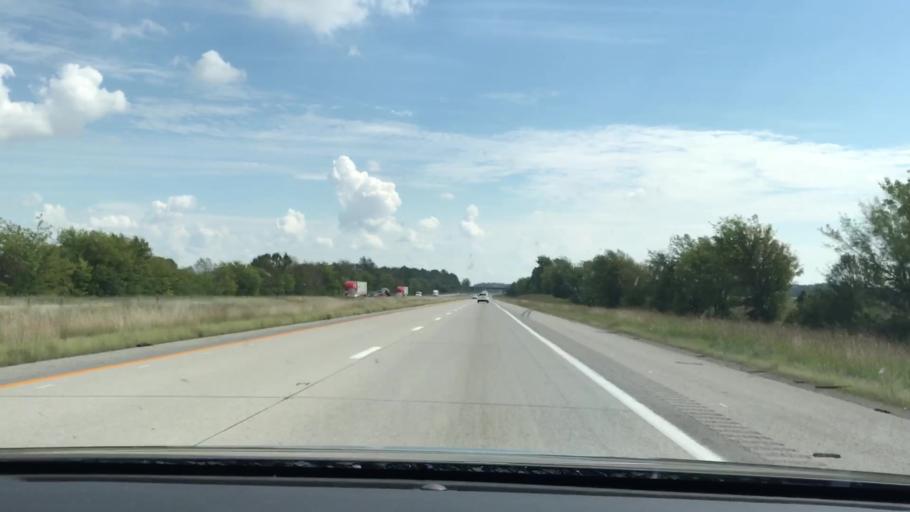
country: US
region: Kentucky
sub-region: Christian County
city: Hopkinsville
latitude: 36.7909
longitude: -87.5940
